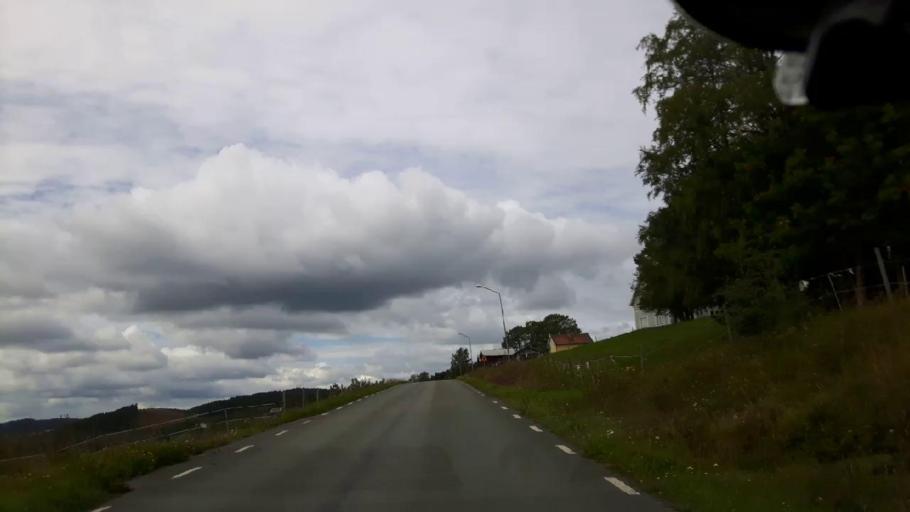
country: SE
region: Jaemtland
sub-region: Krokoms Kommun
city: Valla
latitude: 63.4847
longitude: 14.0445
